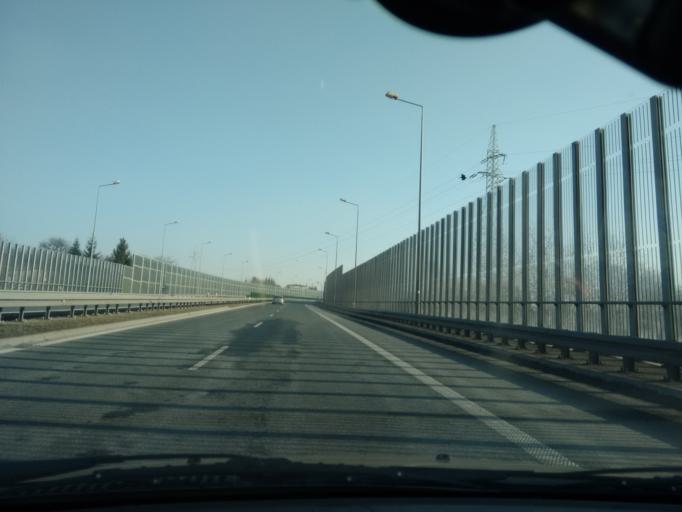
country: PL
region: Silesian Voivodeship
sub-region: Bielsko-Biala
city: Bielsko-Biala
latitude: 49.8493
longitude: 19.0522
